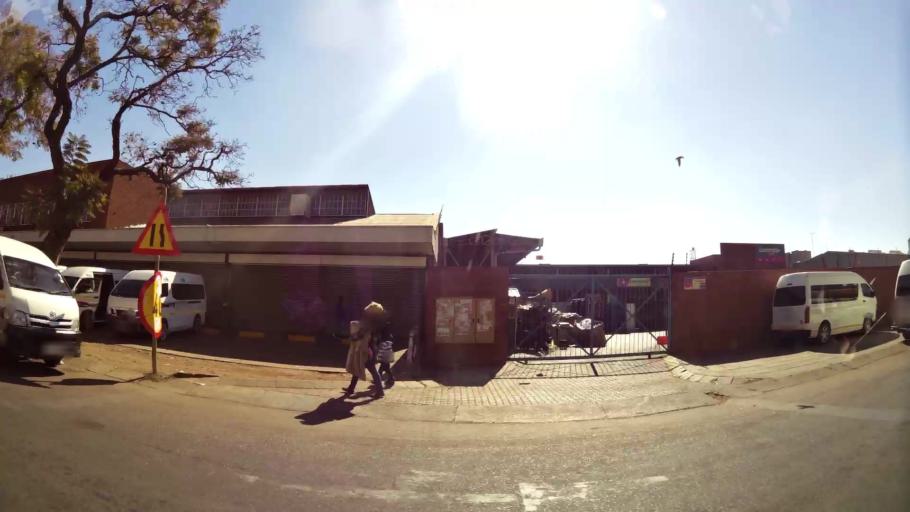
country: ZA
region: Gauteng
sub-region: City of Tshwane Metropolitan Municipality
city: Pretoria
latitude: -25.7417
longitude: 28.1918
